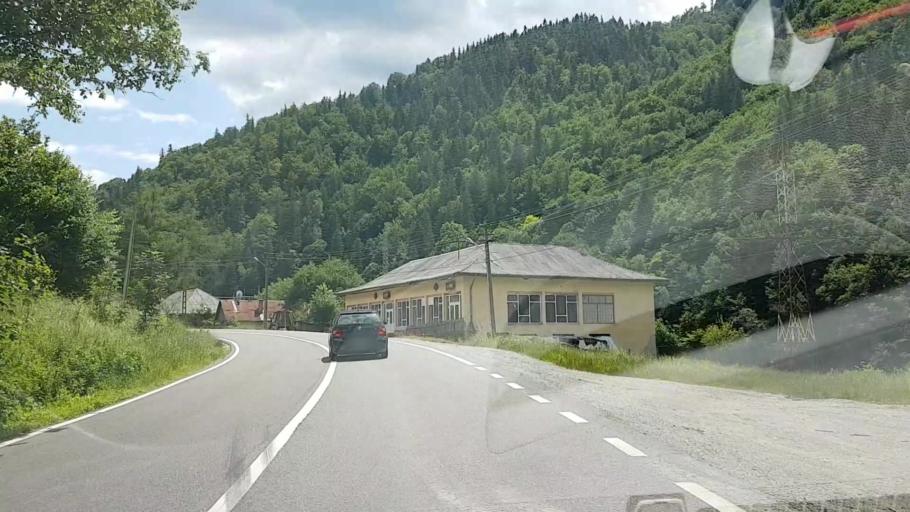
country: RO
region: Suceava
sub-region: Comuna Crucea
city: Crucea
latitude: 47.2842
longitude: 25.6367
